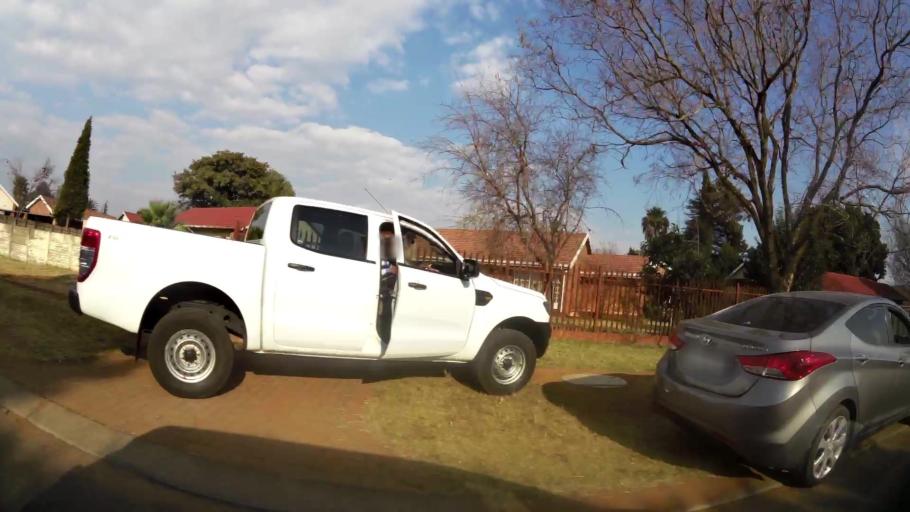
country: ZA
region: Gauteng
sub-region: Ekurhuleni Metropolitan Municipality
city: Benoni
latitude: -26.1250
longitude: 28.3709
